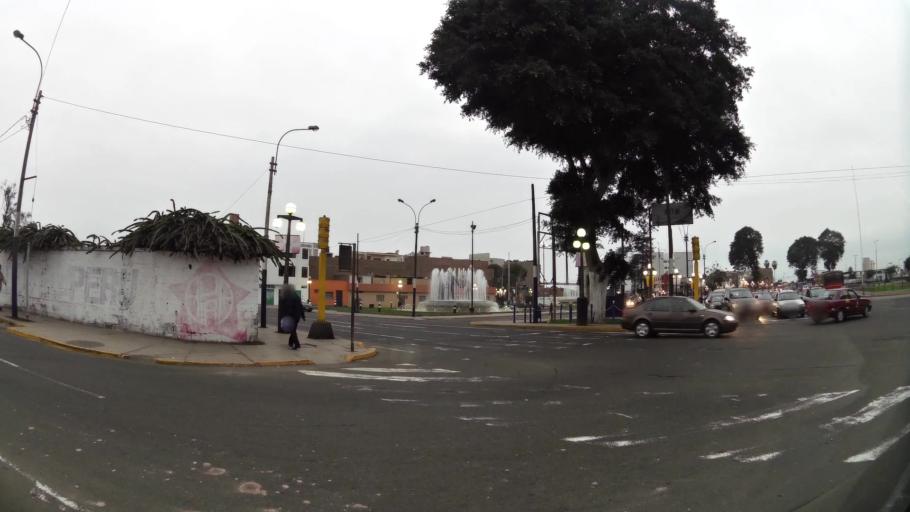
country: PE
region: Lima
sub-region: Lima
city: Surco
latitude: -12.1645
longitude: -77.0215
